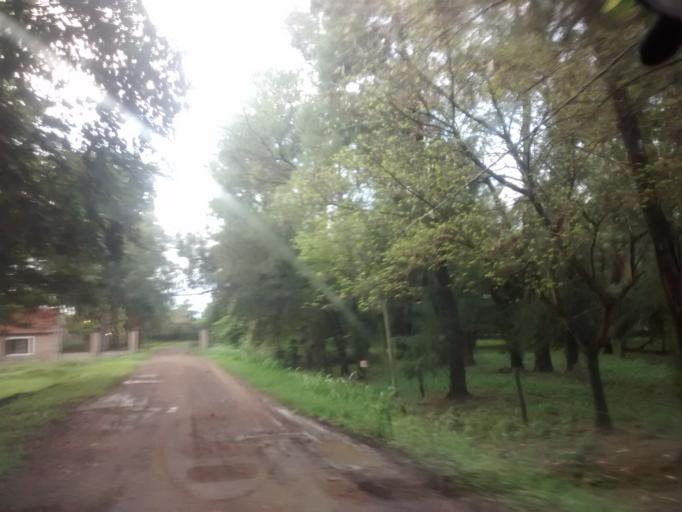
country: AR
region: Chaco
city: Fontana
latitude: -27.4214
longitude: -59.0057
